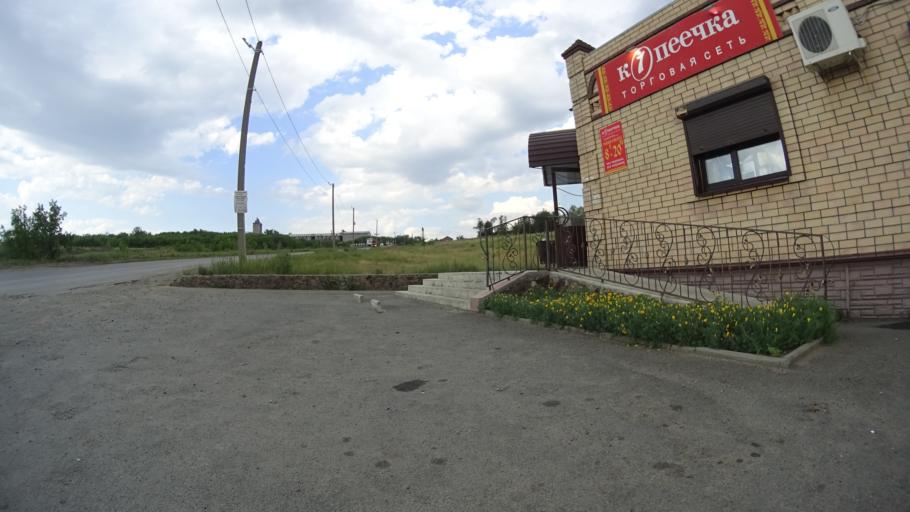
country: RU
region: Chelyabinsk
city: Troitsk
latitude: 54.1008
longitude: 61.5917
